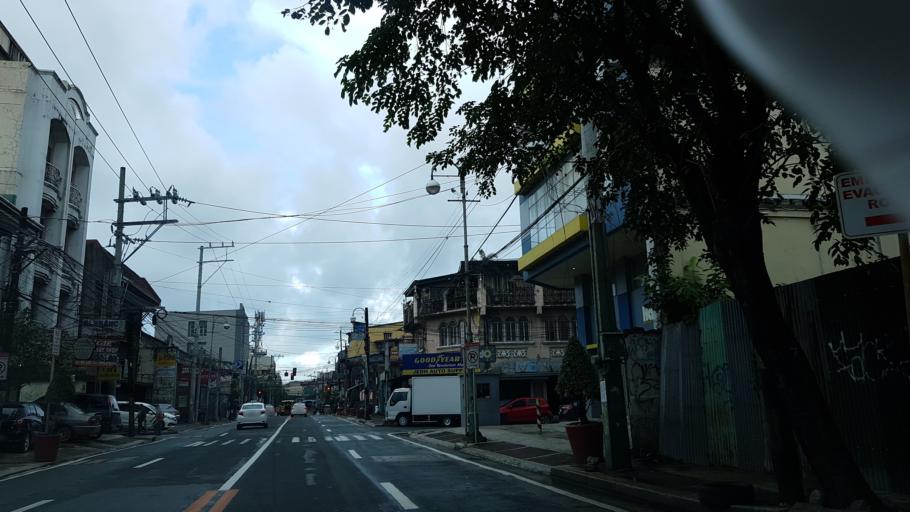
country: PH
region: Metro Manila
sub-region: Makati City
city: Makati City
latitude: 14.5713
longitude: 121.0185
